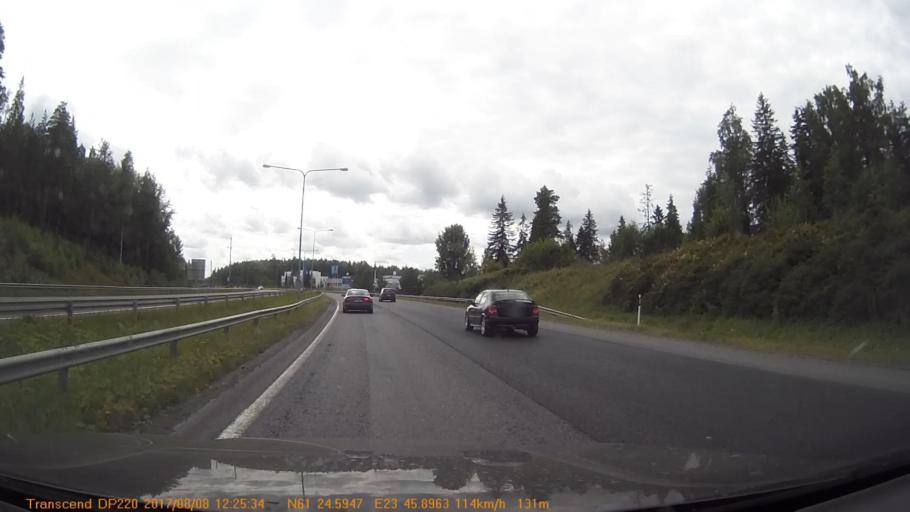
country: FI
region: Pirkanmaa
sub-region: Tampere
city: Tampere
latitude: 61.4097
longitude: 23.7650
